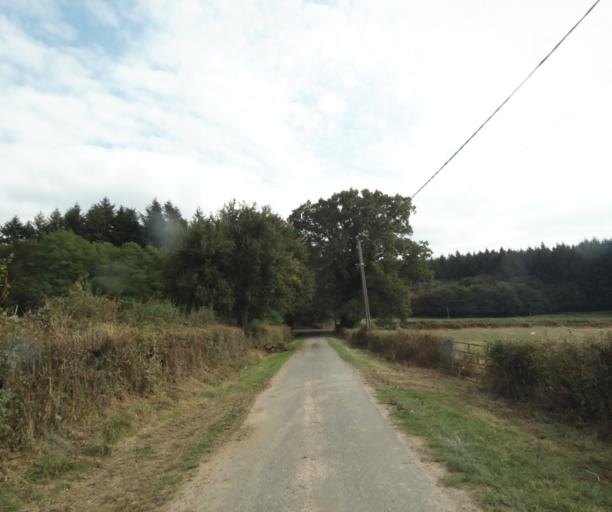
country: FR
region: Bourgogne
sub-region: Departement de Saone-et-Loire
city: Palinges
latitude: 46.5136
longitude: 4.2783
